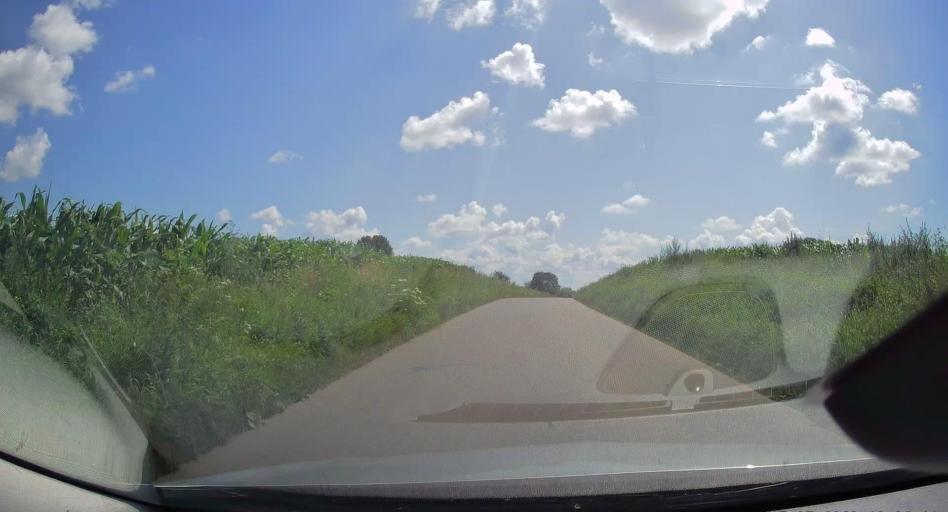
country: PL
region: Subcarpathian Voivodeship
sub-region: Powiat jaroslawski
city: Sosnica
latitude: 49.8489
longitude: 22.8846
